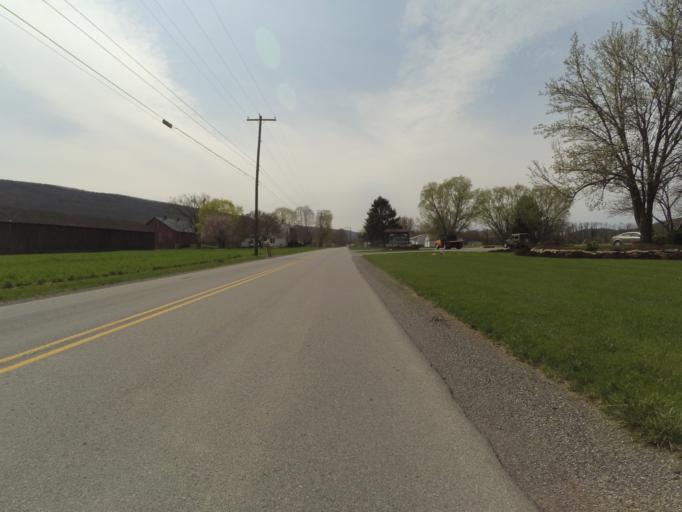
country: US
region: Pennsylvania
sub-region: Clinton County
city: Dunnstown
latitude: 41.1464
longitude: -77.3926
